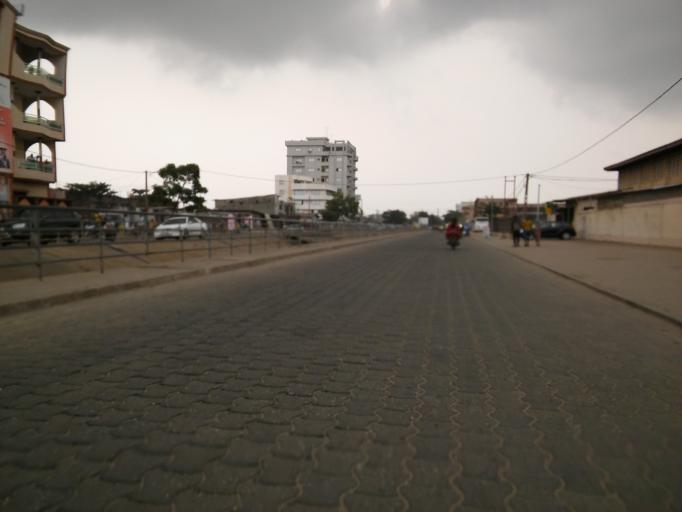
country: BJ
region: Littoral
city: Cotonou
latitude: 6.3762
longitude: 2.4157
